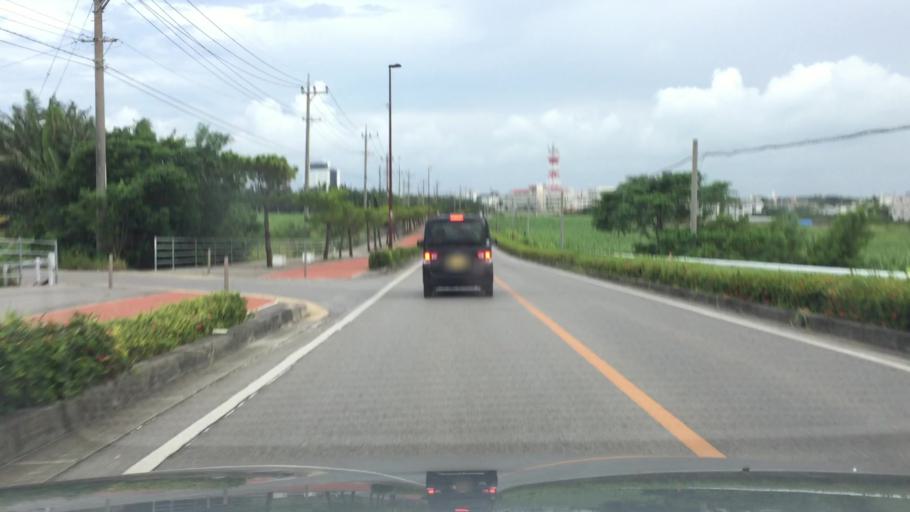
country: JP
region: Okinawa
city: Ishigaki
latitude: 24.3570
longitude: 124.1571
